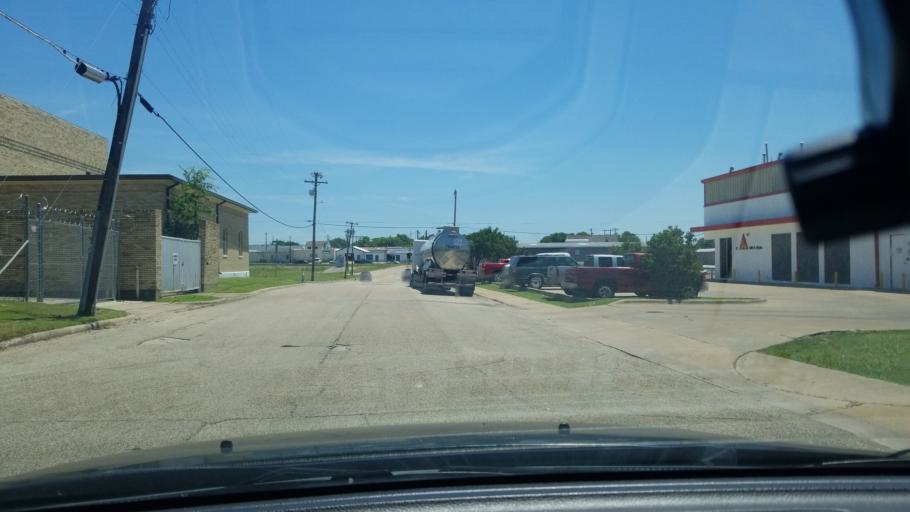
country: US
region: Texas
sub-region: Dallas County
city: Mesquite
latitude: 32.7694
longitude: -96.6020
